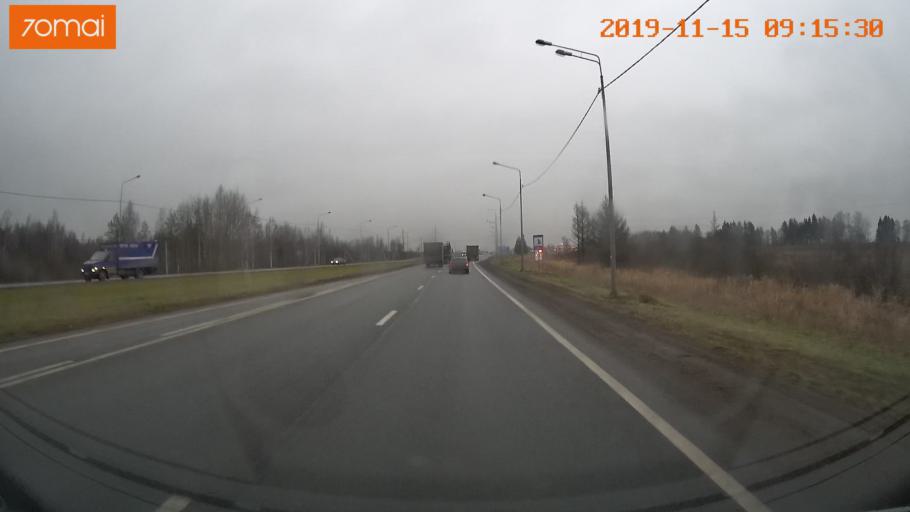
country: RU
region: Vologda
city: Tonshalovo
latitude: 59.2396
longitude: 37.9674
